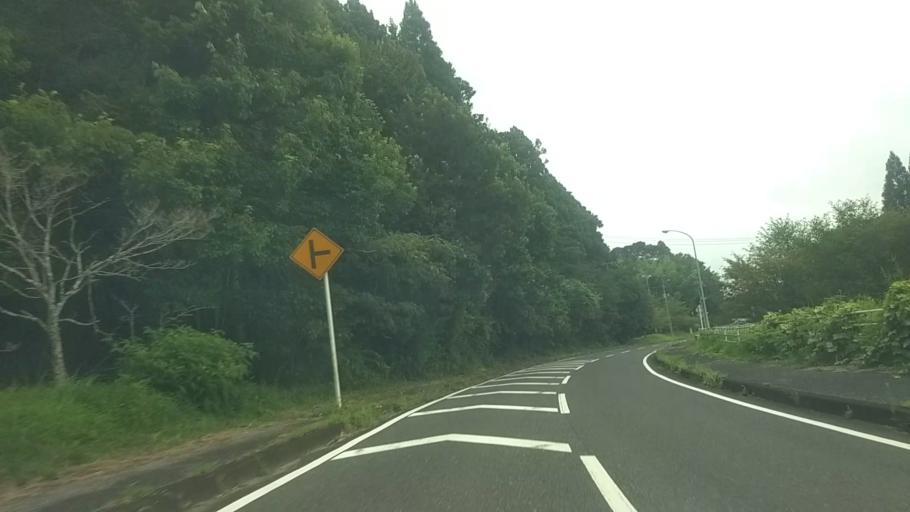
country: JP
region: Chiba
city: Kawaguchi
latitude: 35.2384
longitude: 140.0858
